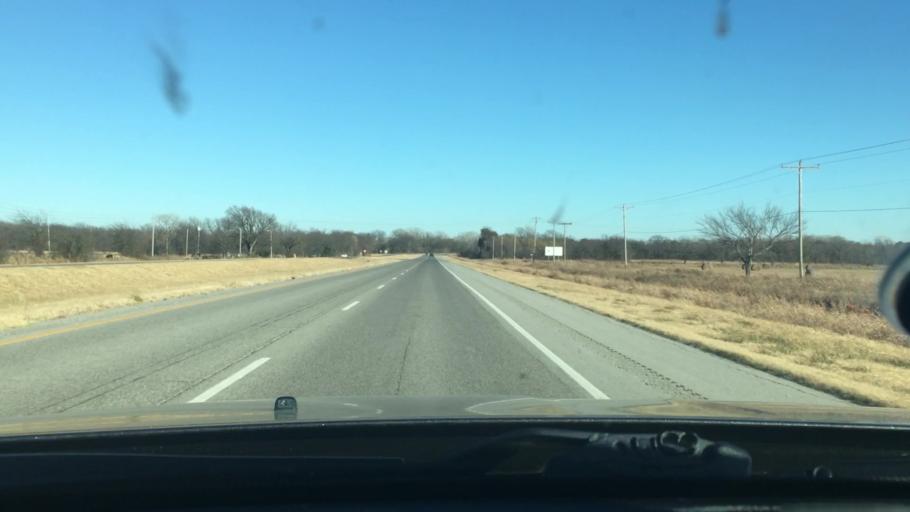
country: US
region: Oklahoma
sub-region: Murray County
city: Davis
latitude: 34.5063
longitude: -97.1588
